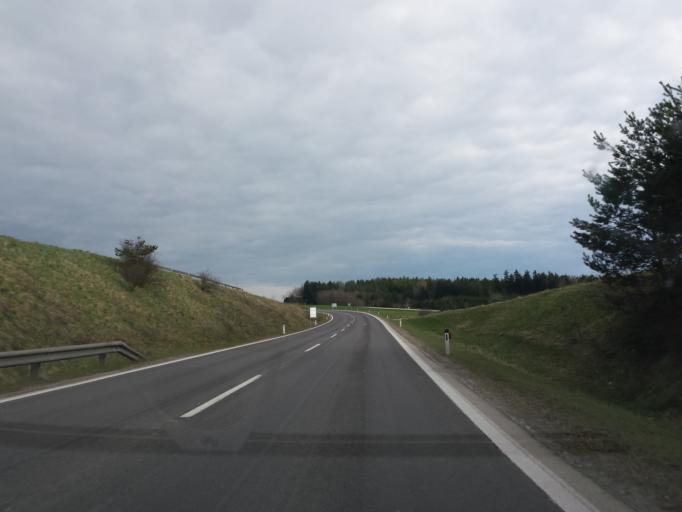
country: AT
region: Lower Austria
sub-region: Politischer Bezirk Krems
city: Krumau am Kamp
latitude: 48.5344
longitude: 15.4037
